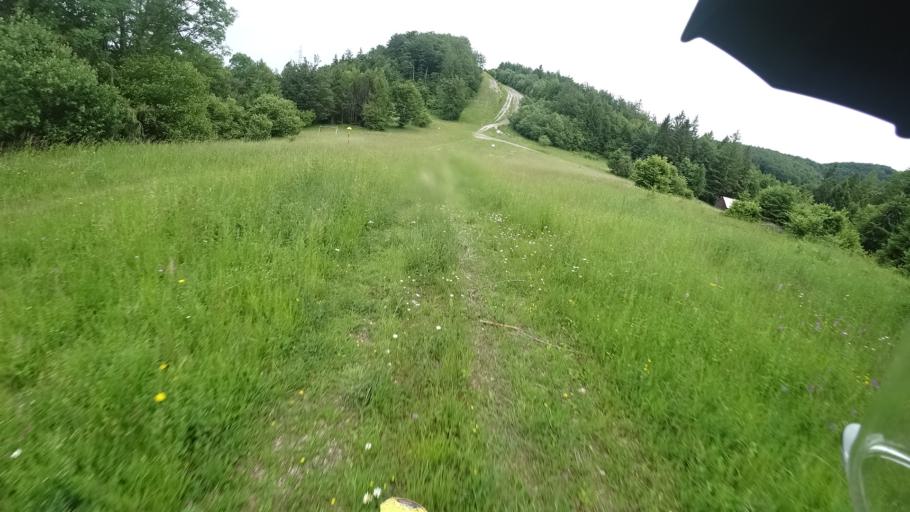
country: HR
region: Primorsko-Goranska
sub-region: Grad Delnice
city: Delnice
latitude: 45.3973
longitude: 14.8179
